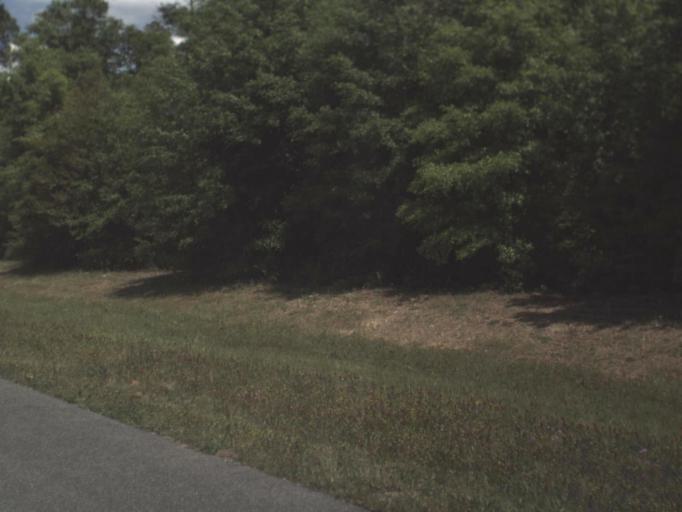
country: US
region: Florida
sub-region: Santa Rosa County
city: Point Baker
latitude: 30.6939
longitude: -87.0531
